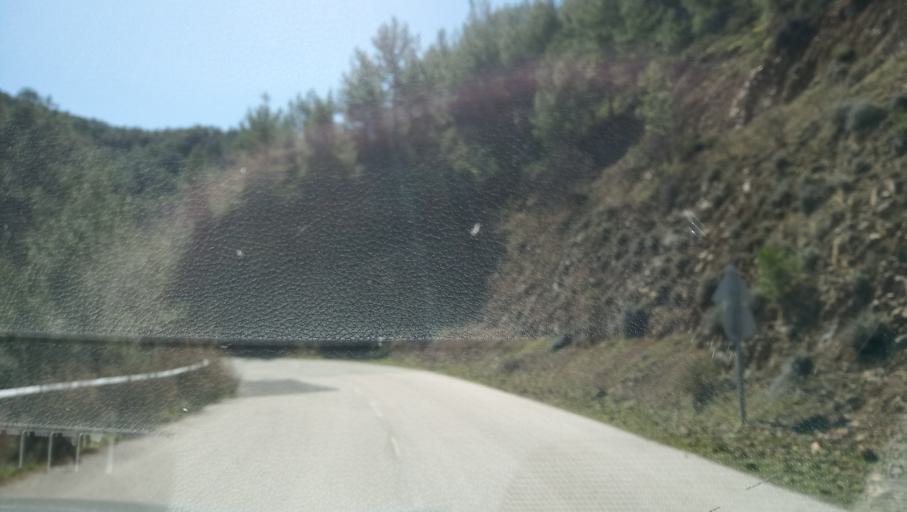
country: CY
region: Lefkosia
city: Lefka
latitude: 35.0657
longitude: 32.7455
